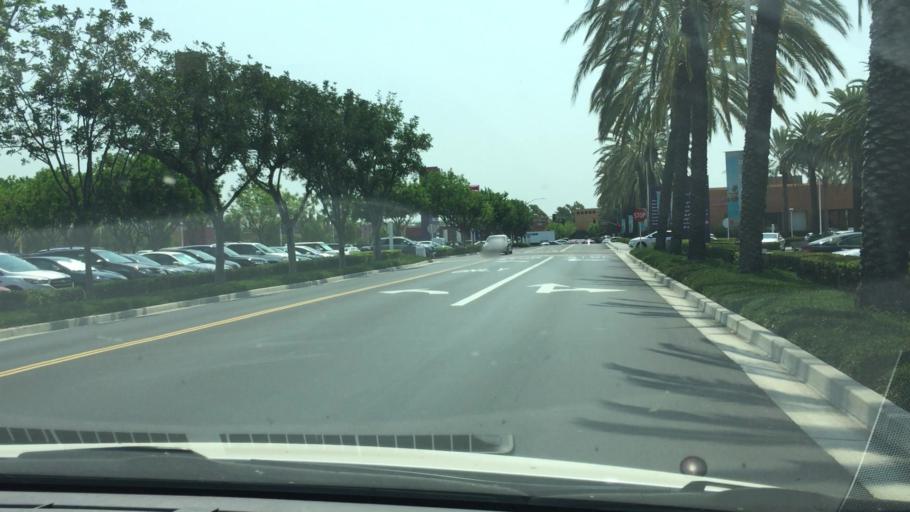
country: US
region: California
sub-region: Orange County
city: Tustin
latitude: 33.7249
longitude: -117.7928
